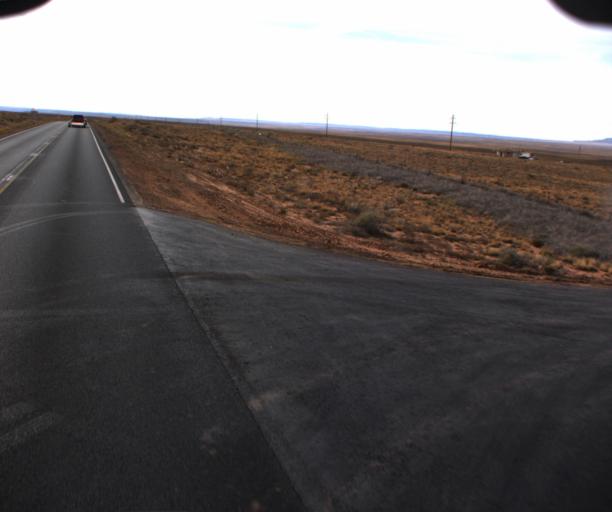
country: US
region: Arizona
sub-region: Apache County
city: Chinle
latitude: 36.0485
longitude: -109.6080
